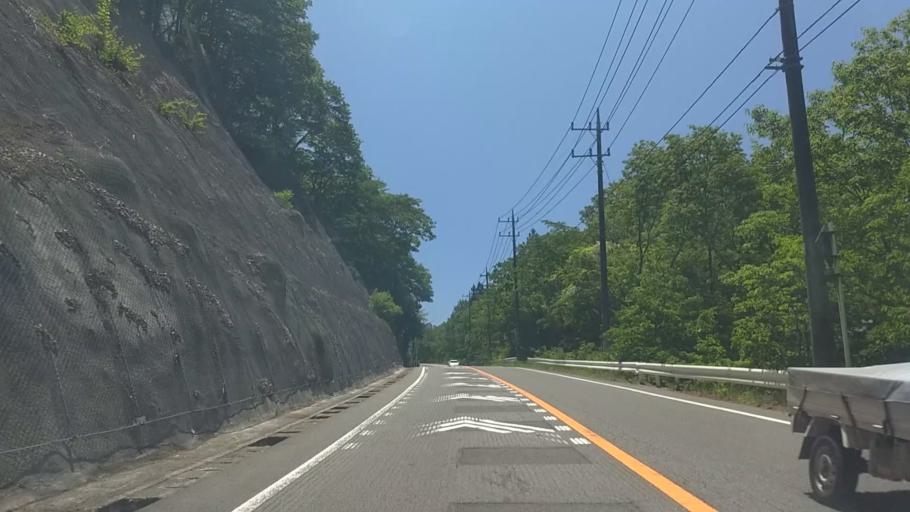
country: JP
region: Yamanashi
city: Nirasaki
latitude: 35.8840
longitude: 138.4283
